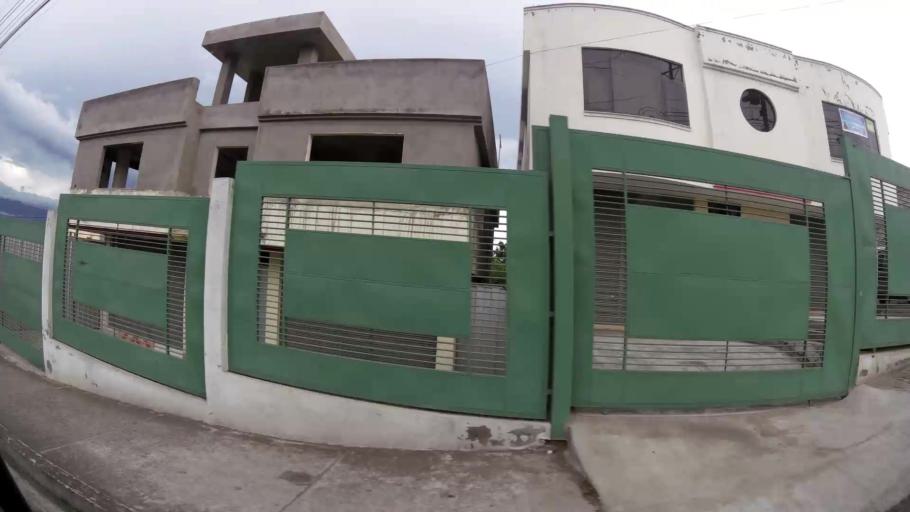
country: EC
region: Tungurahua
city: Ambato
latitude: -1.2727
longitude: -78.6337
